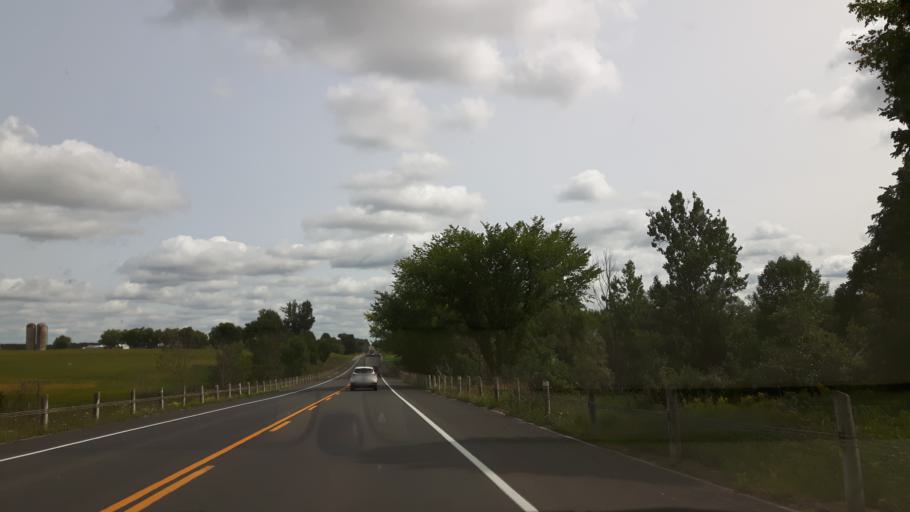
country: CA
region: Ontario
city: Bluewater
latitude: 43.6078
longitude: -81.5183
